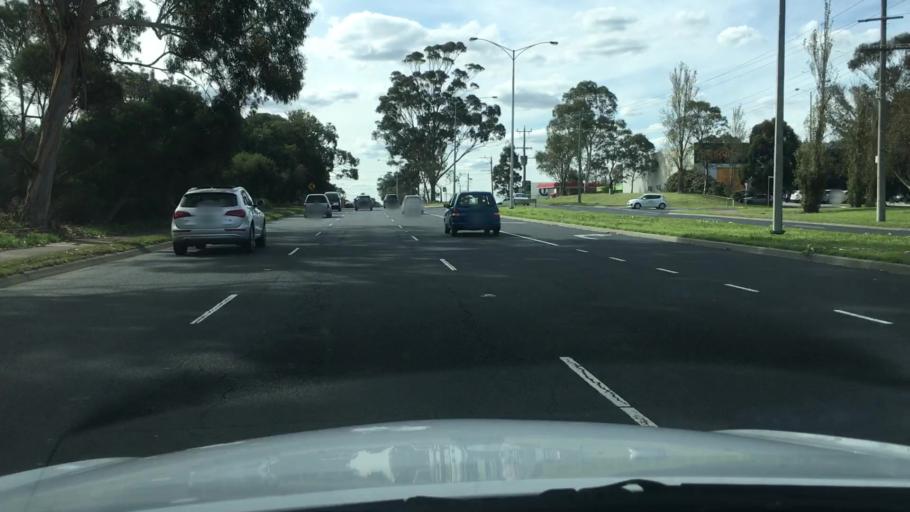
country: AU
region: Victoria
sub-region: Kingston
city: Dingley Village
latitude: -37.9882
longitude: 145.1450
